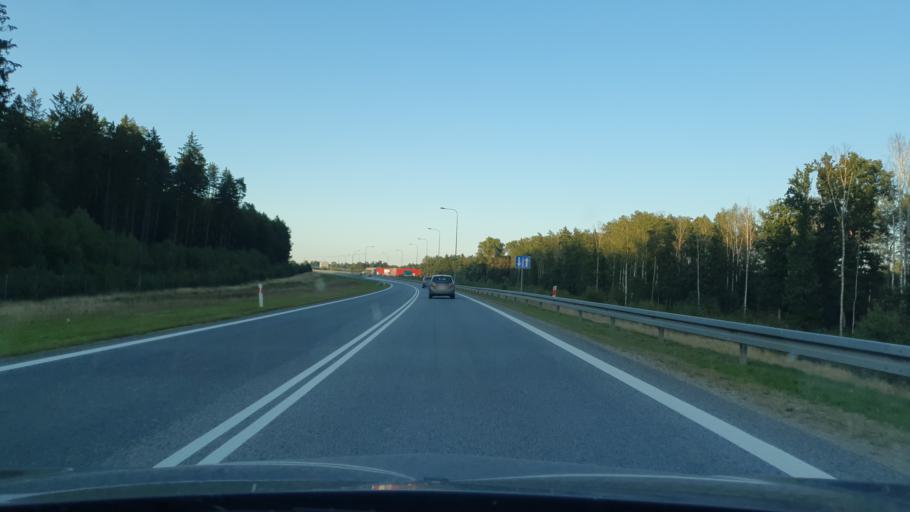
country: PL
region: Pomeranian Voivodeship
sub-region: Slupsk
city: Slupsk
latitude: 54.4415
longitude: 17.0757
